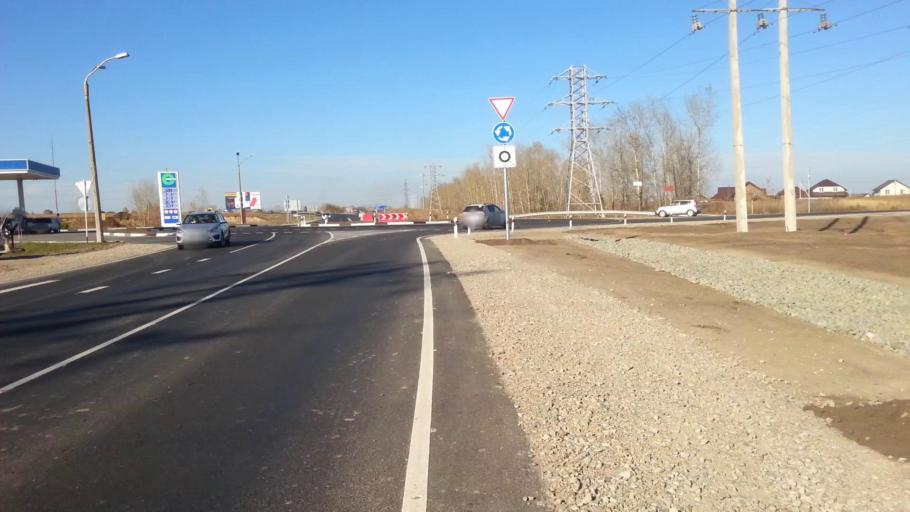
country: RU
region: Altai Krai
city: Sannikovo
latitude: 53.3362
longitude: 83.9386
